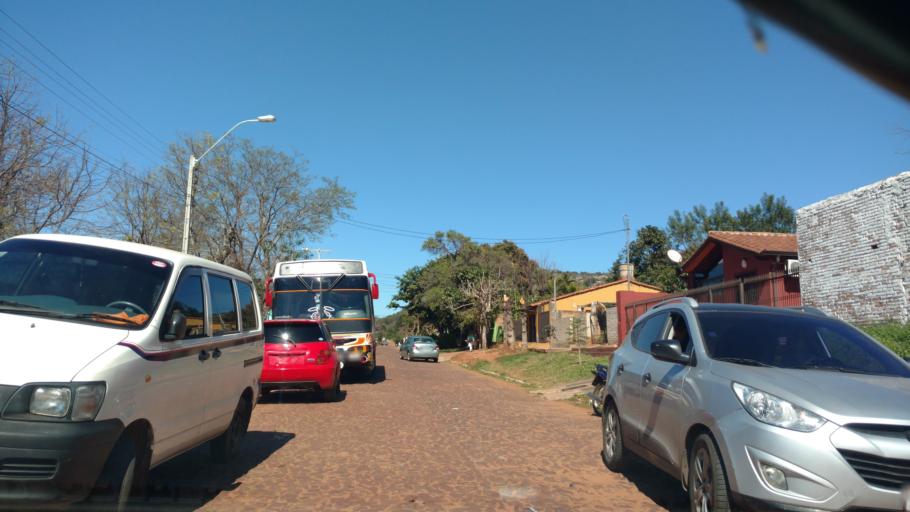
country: PY
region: Paraguari
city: Yaguaron
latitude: -25.5624
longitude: -57.2908
